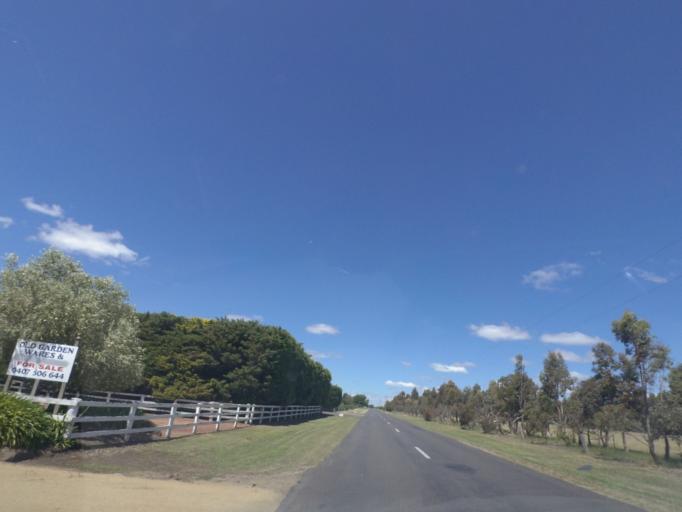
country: AU
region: Victoria
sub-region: Mount Alexander
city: Castlemaine
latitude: -37.2365
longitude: 144.4035
